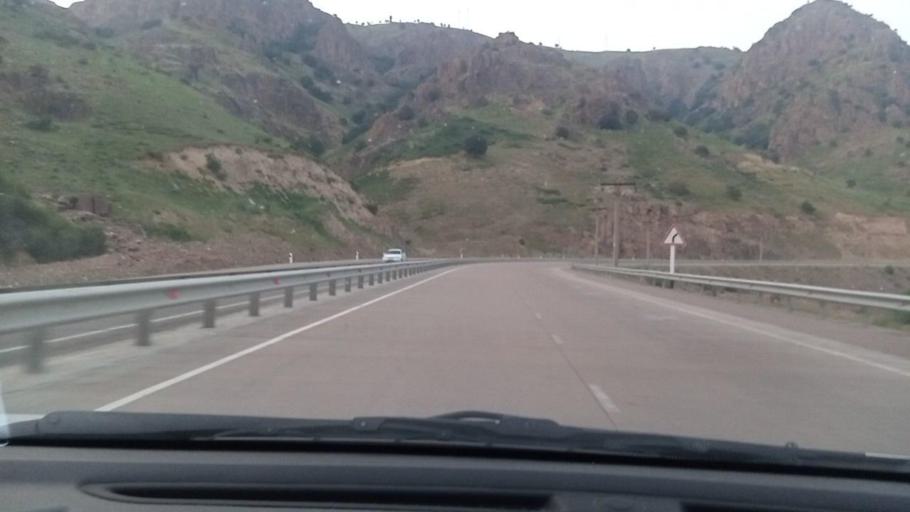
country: UZ
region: Toshkent
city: Angren
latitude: 41.1354
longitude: 70.3731
